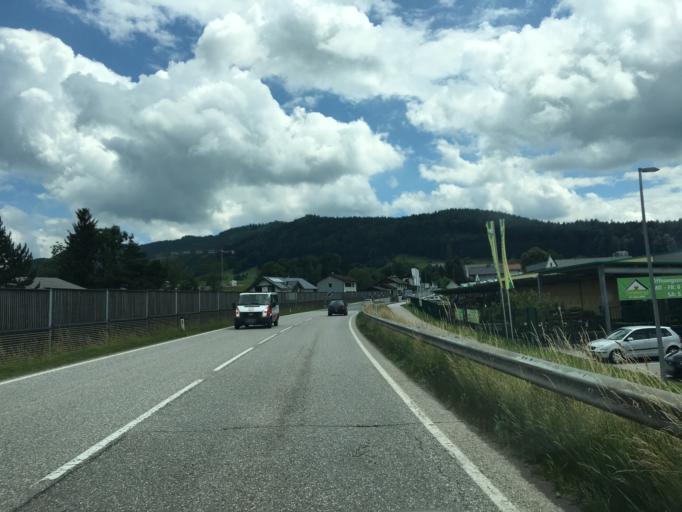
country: AT
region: Salzburg
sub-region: Politischer Bezirk Salzburg-Umgebung
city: Hof bei Salzburg
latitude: 47.8237
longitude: 13.2002
